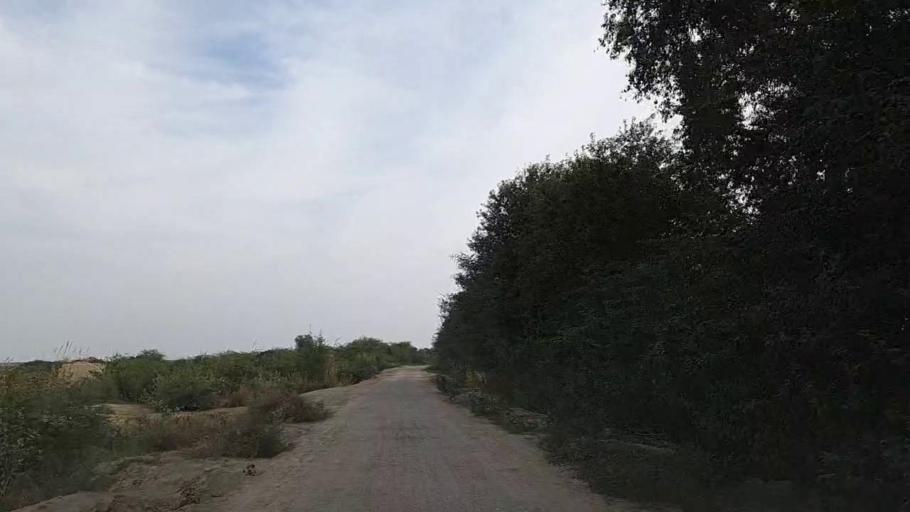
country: PK
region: Sindh
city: Jam Sahib
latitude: 26.4382
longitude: 68.6279
